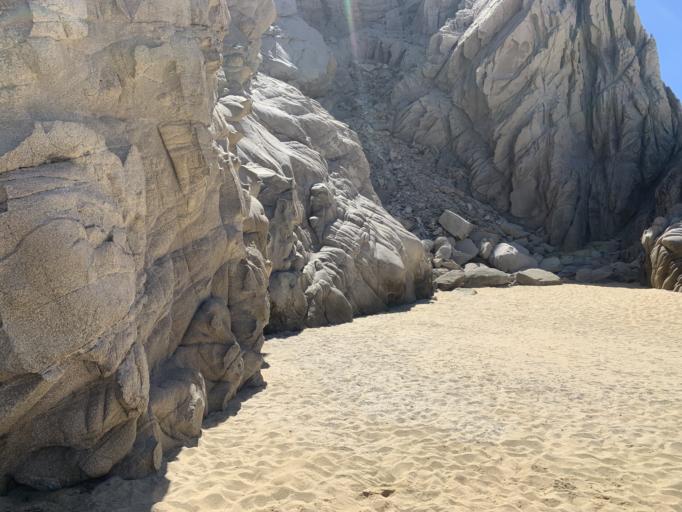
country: MX
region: Baja California Sur
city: Cabo San Lucas
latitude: 22.8767
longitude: -109.8958
